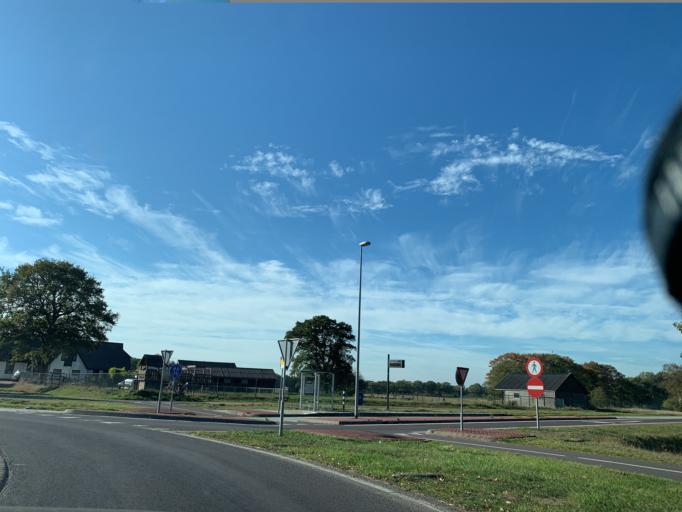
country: NL
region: Drenthe
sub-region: Gemeente Tynaarlo
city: Zuidlaren
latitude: 53.0855
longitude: 6.6534
